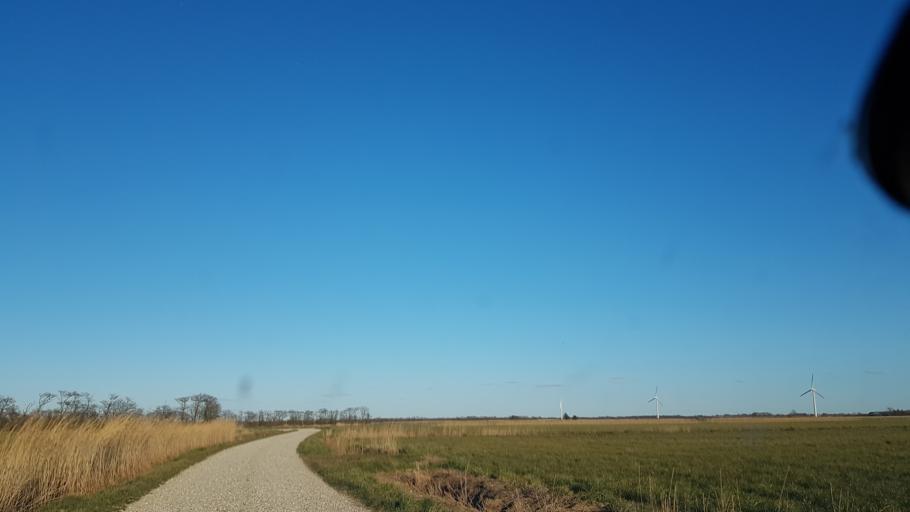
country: DK
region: South Denmark
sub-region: Esbjerg Kommune
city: Bramming
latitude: 55.4144
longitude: 8.6586
